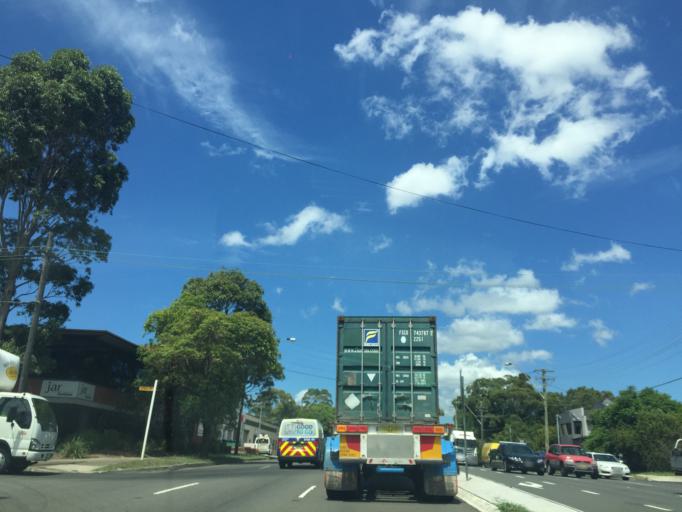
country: AU
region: New South Wales
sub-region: Strathfield
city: Strathfield South
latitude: -33.8961
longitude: 151.0661
